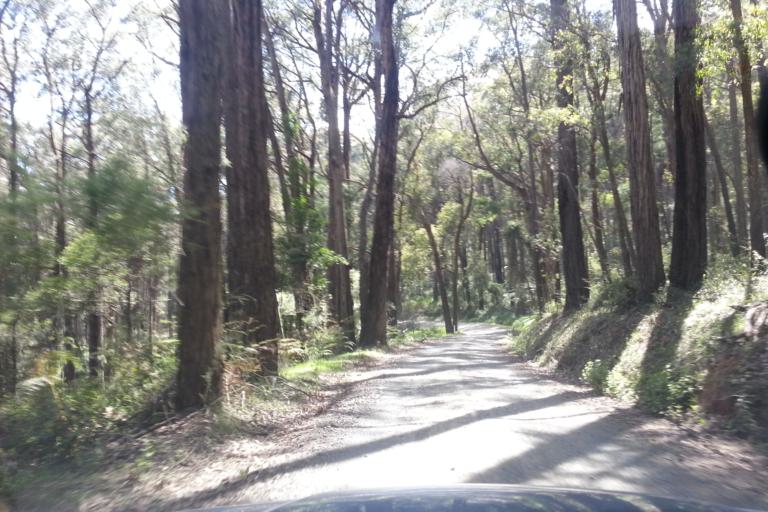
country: AU
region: Victoria
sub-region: Cardinia
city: Gembrook
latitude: -37.9483
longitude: 145.5798
